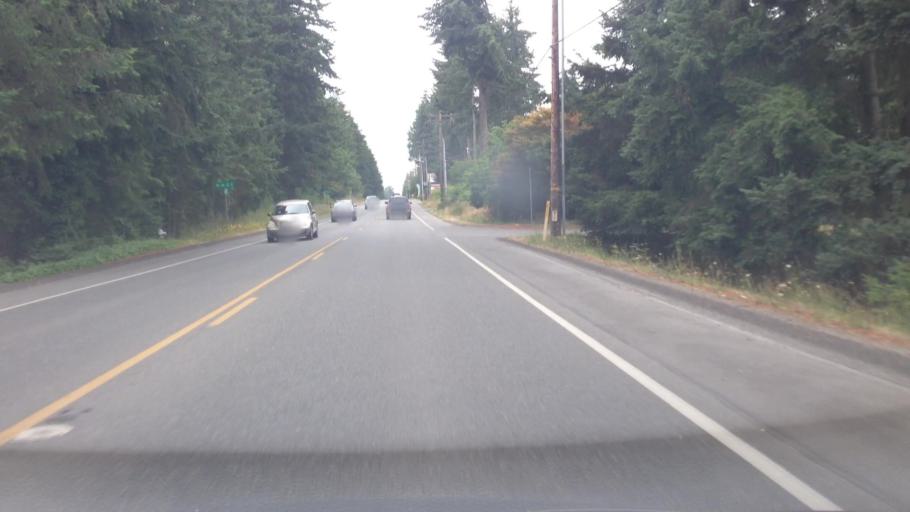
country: US
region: Washington
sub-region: Pierce County
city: South Hill
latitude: 47.1111
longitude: -122.3004
